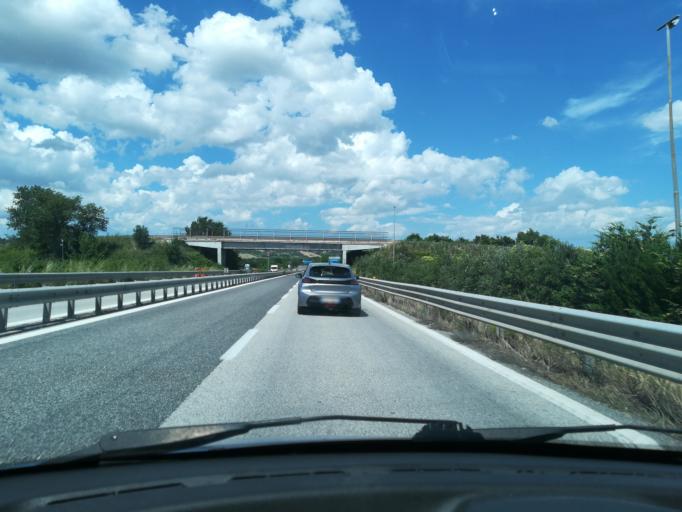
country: IT
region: The Marches
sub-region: Provincia di Macerata
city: Urbisaglia
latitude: 43.2208
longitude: 13.3387
